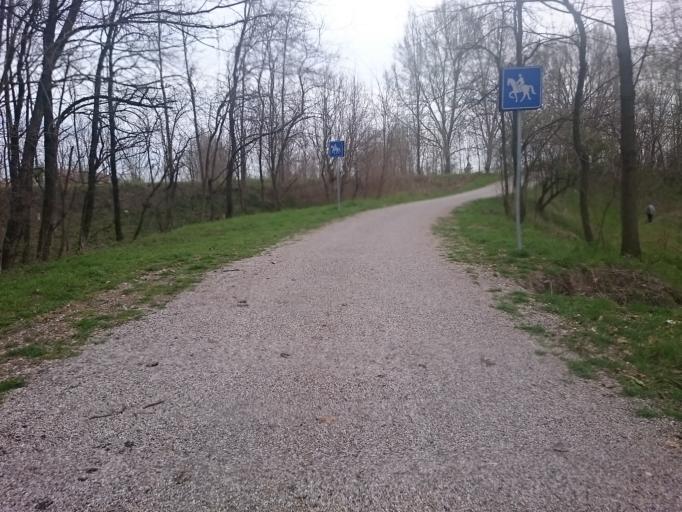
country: IT
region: Veneto
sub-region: Provincia di Padova
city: Saletto
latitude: 45.4776
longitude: 11.8539
